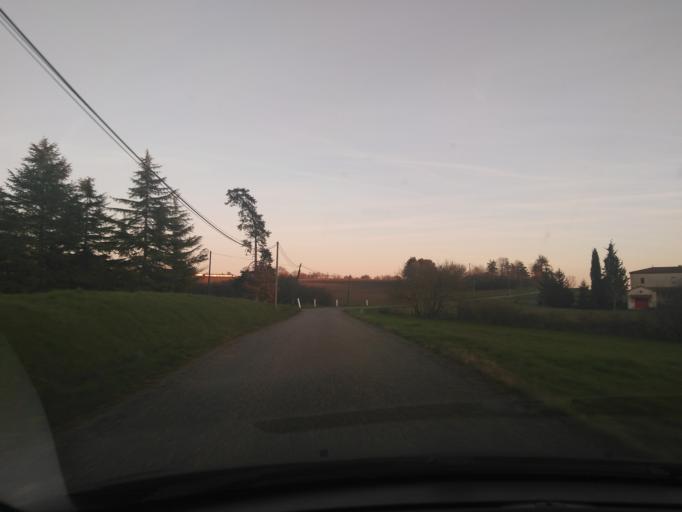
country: FR
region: Aquitaine
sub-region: Departement du Lot-et-Garonne
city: Saint-Hilaire
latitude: 44.4777
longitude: 0.7106
